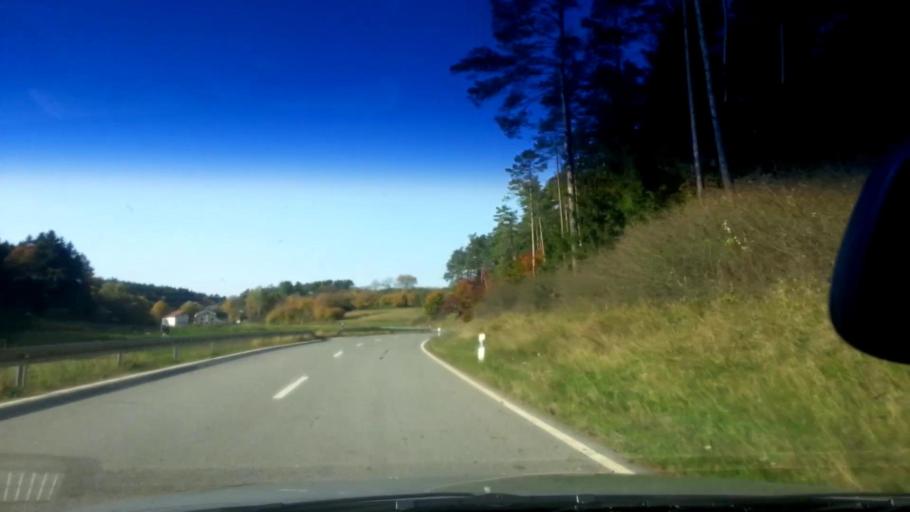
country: DE
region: Bavaria
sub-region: Upper Franconia
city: Stadelhofen
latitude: 49.9750
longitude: 11.1868
